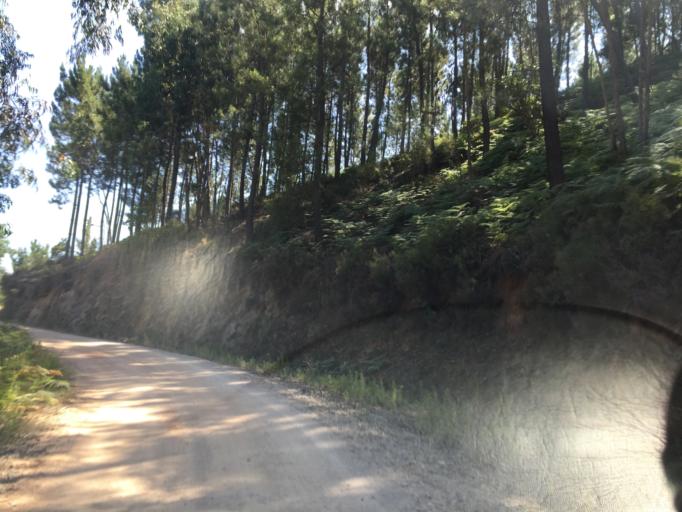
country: PT
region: Leiria
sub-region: Pedrogao Grande
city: Pedrogao Grande
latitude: 39.9301
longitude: -8.1241
